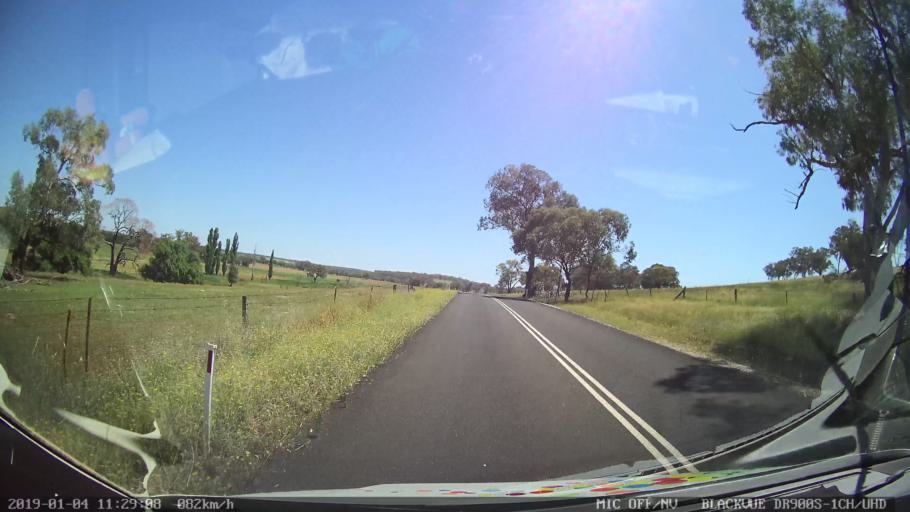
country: AU
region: New South Wales
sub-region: Cabonne
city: Molong
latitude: -33.0915
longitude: 148.7730
